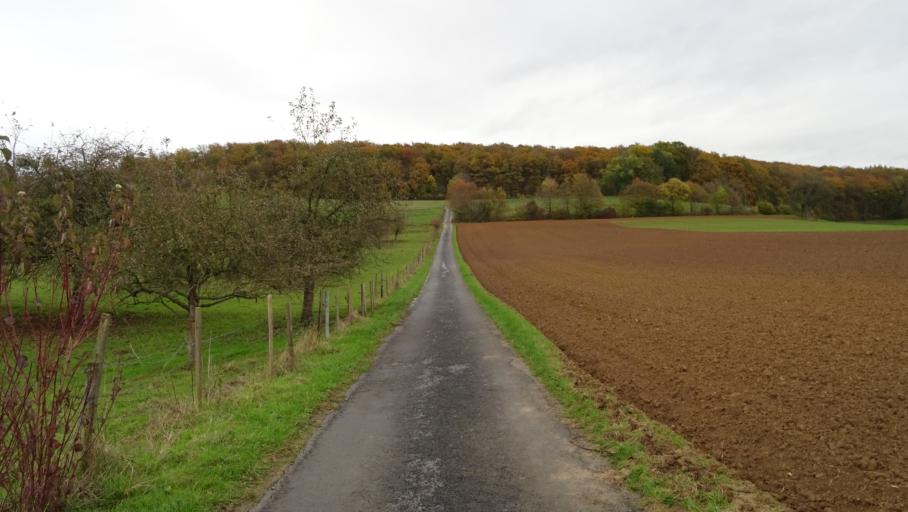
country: DE
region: Baden-Wuerttemberg
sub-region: Karlsruhe Region
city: Obrigheim
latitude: 49.3733
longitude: 9.0902
